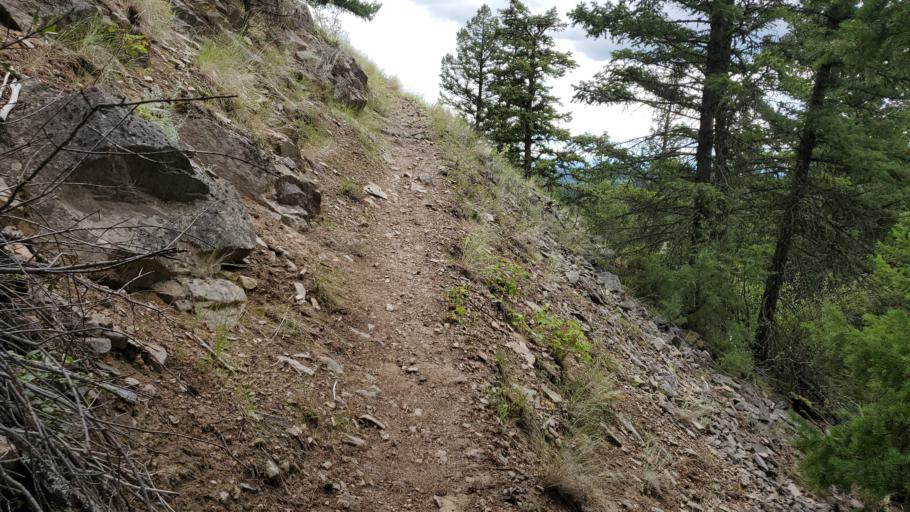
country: CA
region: British Columbia
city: Cache Creek
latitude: 51.4761
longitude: -121.3683
